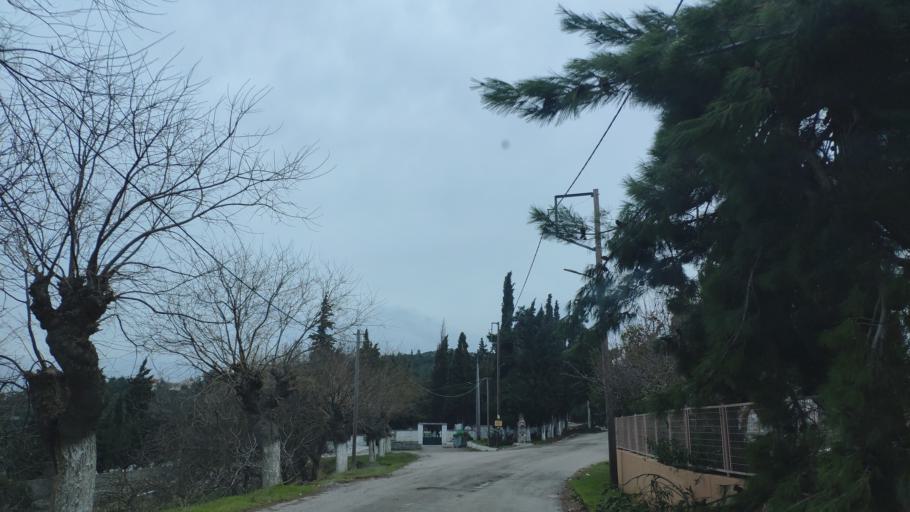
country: GR
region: Attica
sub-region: Nomarchia Dytikis Attikis
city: Vilia
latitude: 38.1658
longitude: 23.3413
